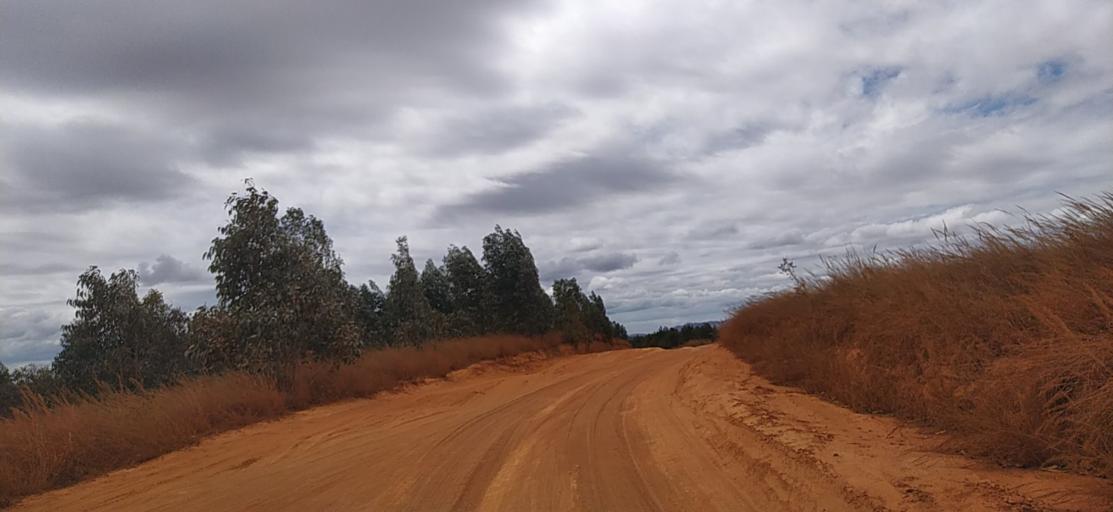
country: MG
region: Alaotra Mangoro
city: Ambatondrazaka
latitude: -18.0458
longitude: 48.2490
